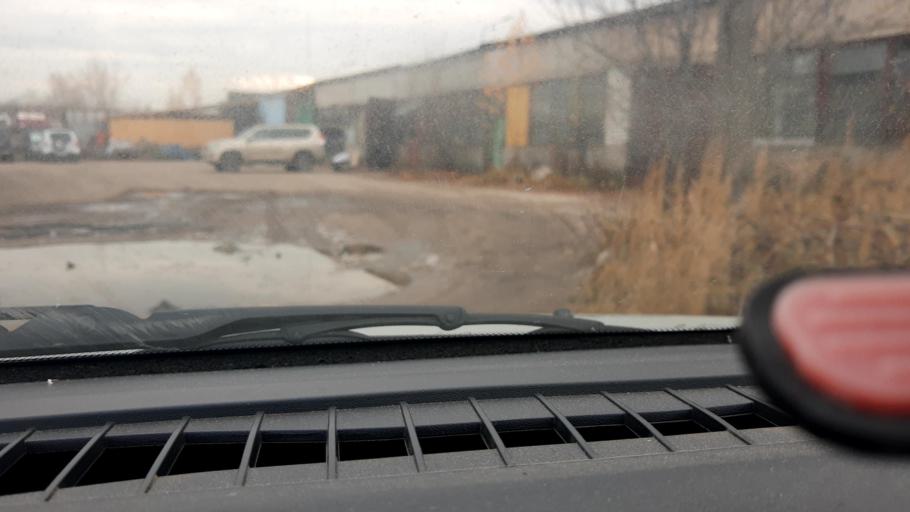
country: RU
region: Nizjnij Novgorod
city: Nizhniy Novgorod
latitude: 56.2915
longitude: 43.8765
